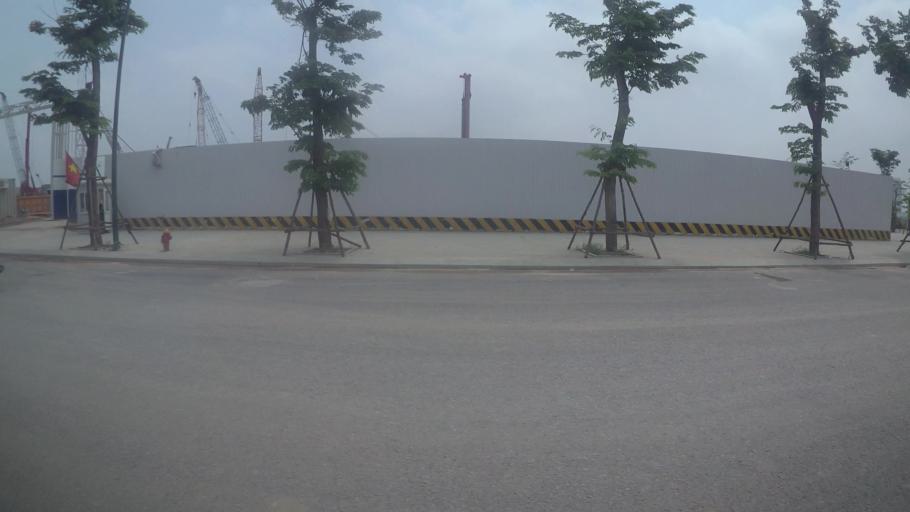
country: VN
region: Ha Noi
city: Tay Ho
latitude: 21.0852
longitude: 105.8017
